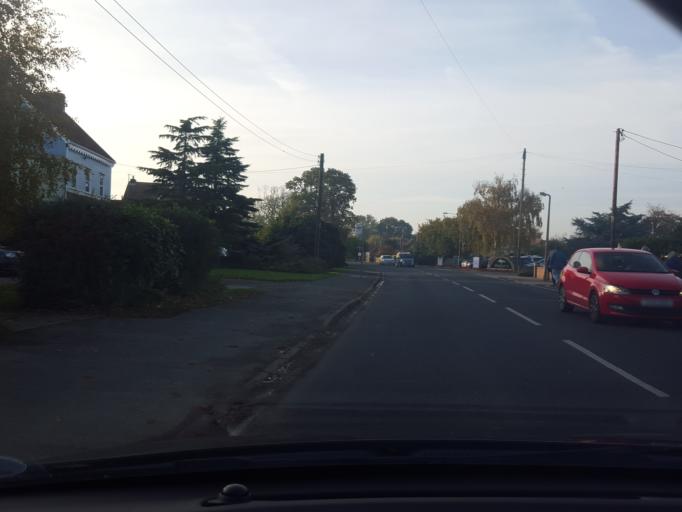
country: GB
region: England
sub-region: Essex
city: Frinton-on-Sea
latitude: 51.8413
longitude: 1.2361
